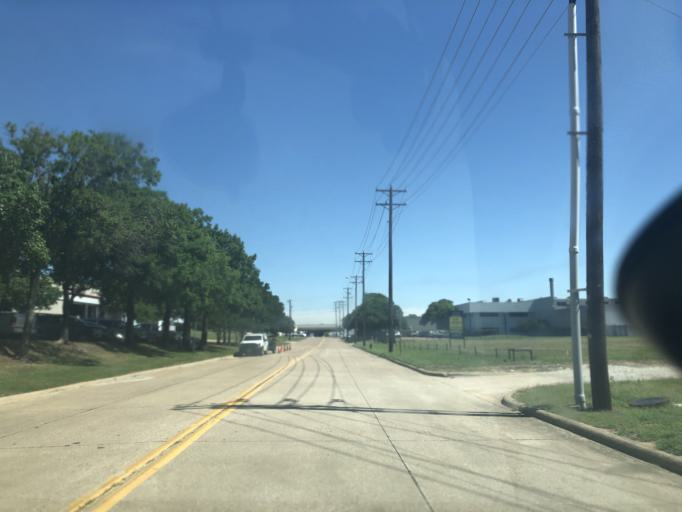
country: US
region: Texas
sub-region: Dallas County
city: Grand Prairie
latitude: 32.7881
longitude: -97.0387
